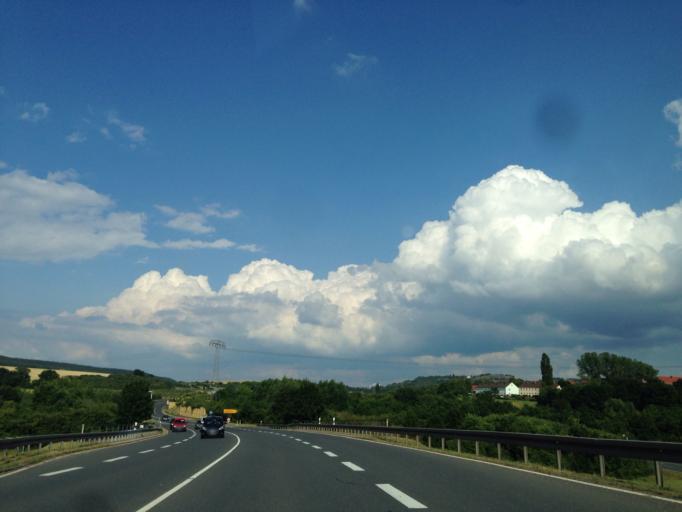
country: DE
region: Thuringia
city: Saalfeld
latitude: 50.6582
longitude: 11.3784
